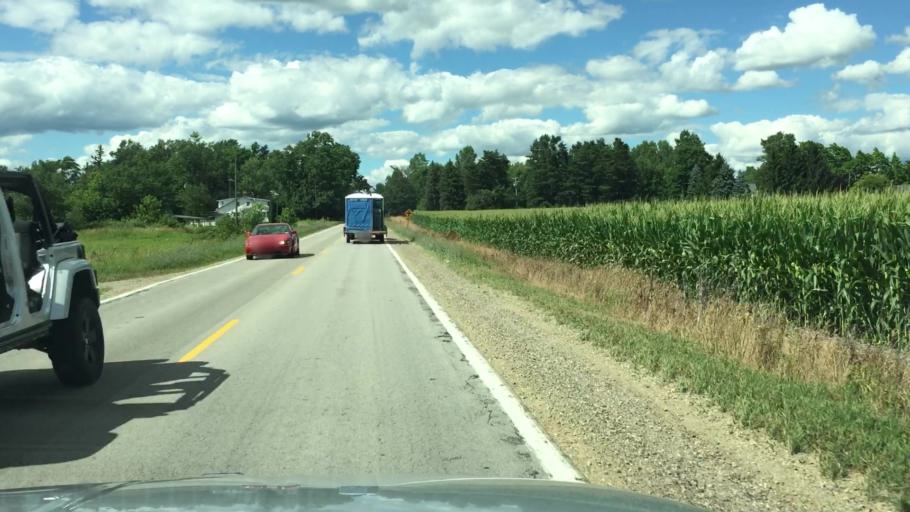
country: US
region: Michigan
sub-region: Macomb County
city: Armada
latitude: 42.8995
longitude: -82.9451
